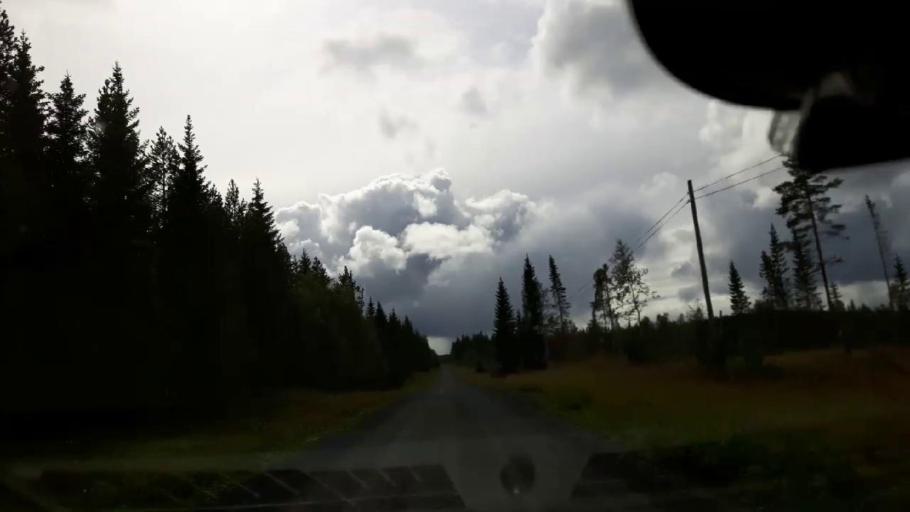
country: SE
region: Jaemtland
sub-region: Krokoms Kommun
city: Valla
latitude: 63.3641
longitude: 13.8670
